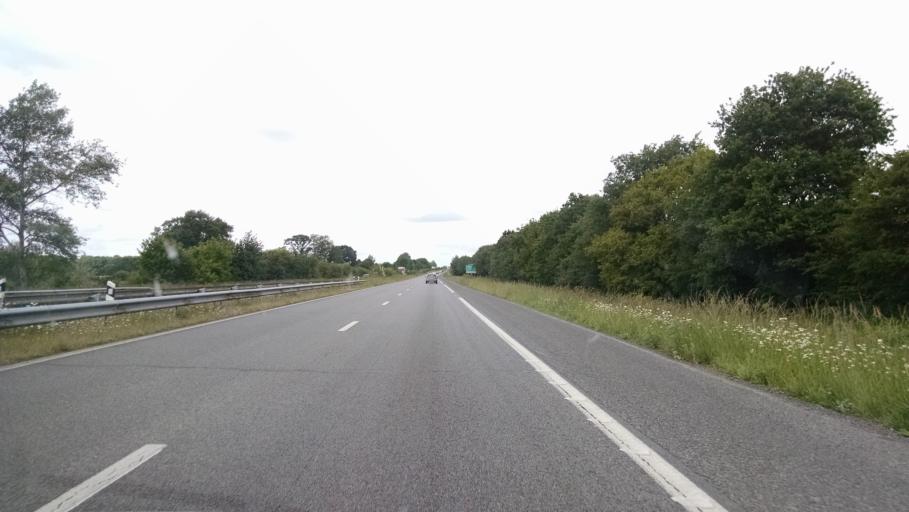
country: FR
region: Pays de la Loire
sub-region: Departement de la Loire-Atlantique
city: Missillac
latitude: 47.4546
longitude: -2.1377
